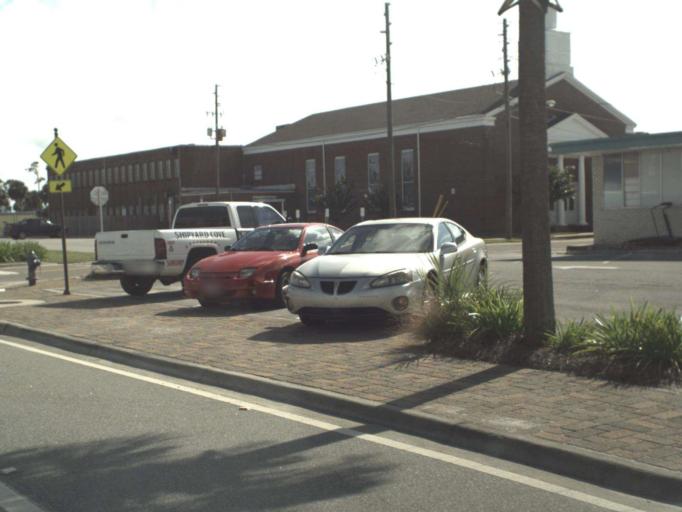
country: US
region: Florida
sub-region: Gulf County
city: Port Saint Joe
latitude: 29.8142
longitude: -85.3044
